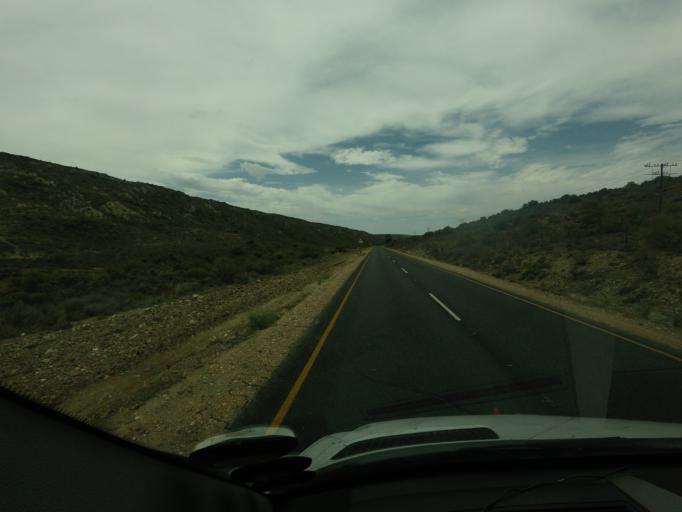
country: ZA
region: Western Cape
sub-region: Overberg District Municipality
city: Swellendam
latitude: -33.8582
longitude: 20.7906
